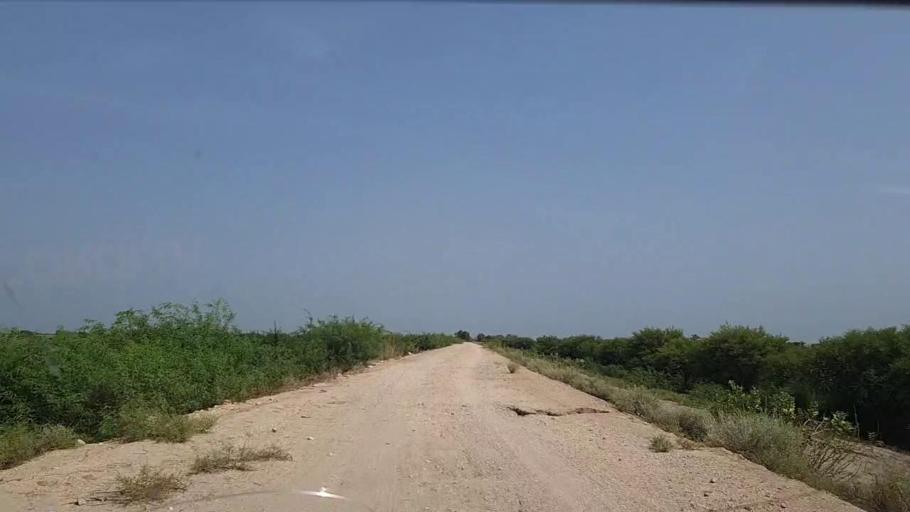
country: PK
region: Sindh
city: Ghotki
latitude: 28.0933
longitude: 69.4070
